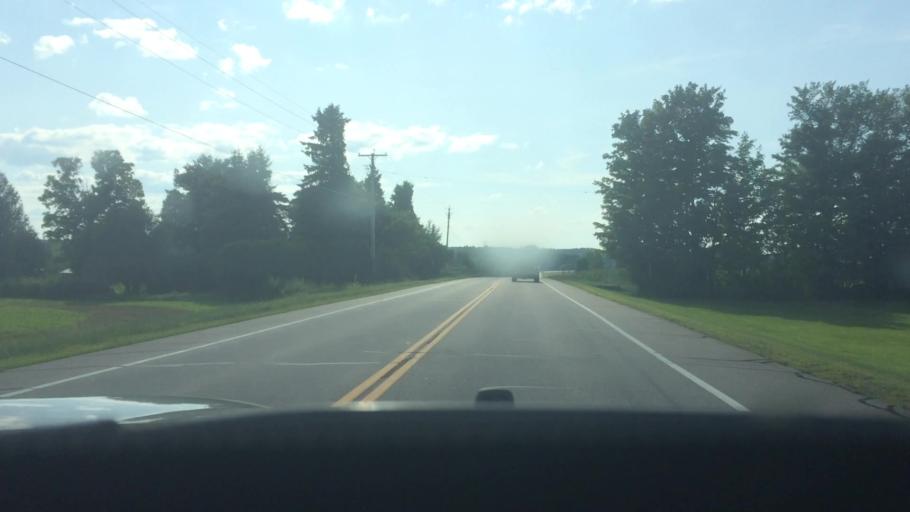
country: US
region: New York
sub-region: Franklin County
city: Malone
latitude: 44.8450
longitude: -74.1796
